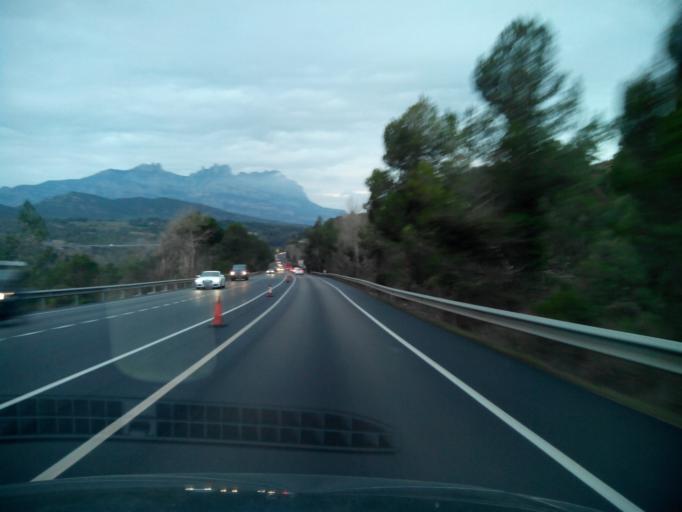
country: ES
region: Catalonia
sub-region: Provincia de Barcelona
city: Viladecavalls
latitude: 41.5848
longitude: 1.9283
